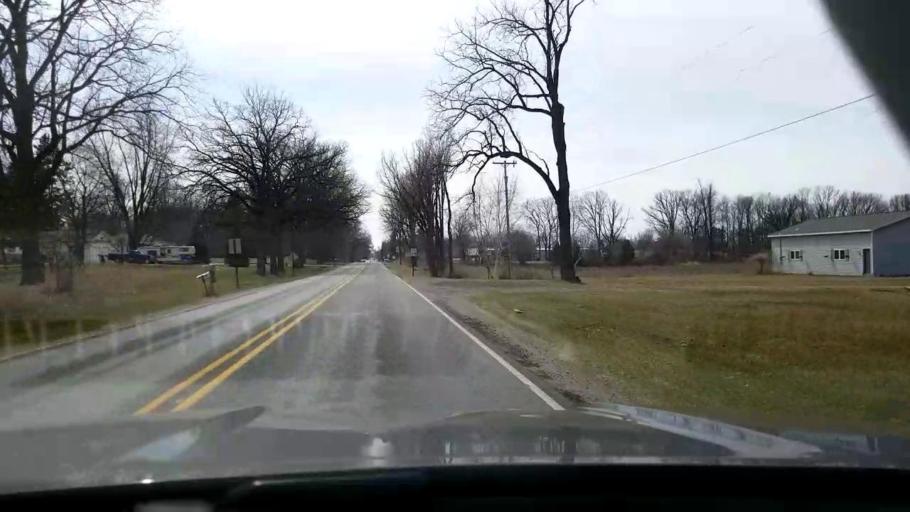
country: US
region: Michigan
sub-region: Jackson County
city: Spring Arbor
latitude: 42.1570
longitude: -84.5190
